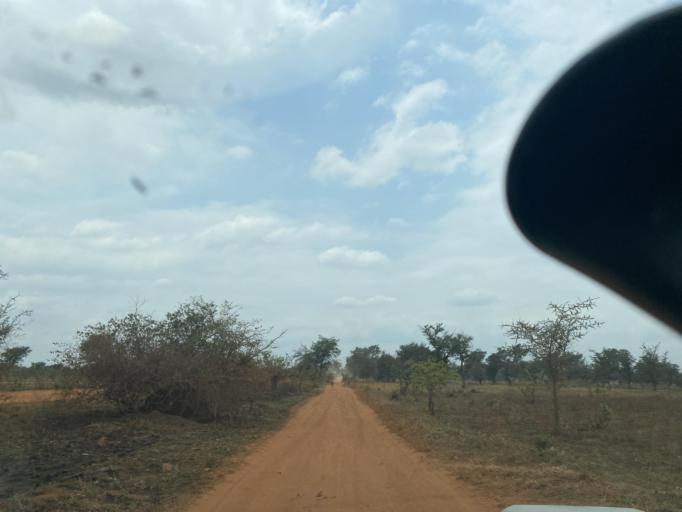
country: ZM
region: Lusaka
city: Chongwe
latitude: -15.4992
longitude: 28.8048
